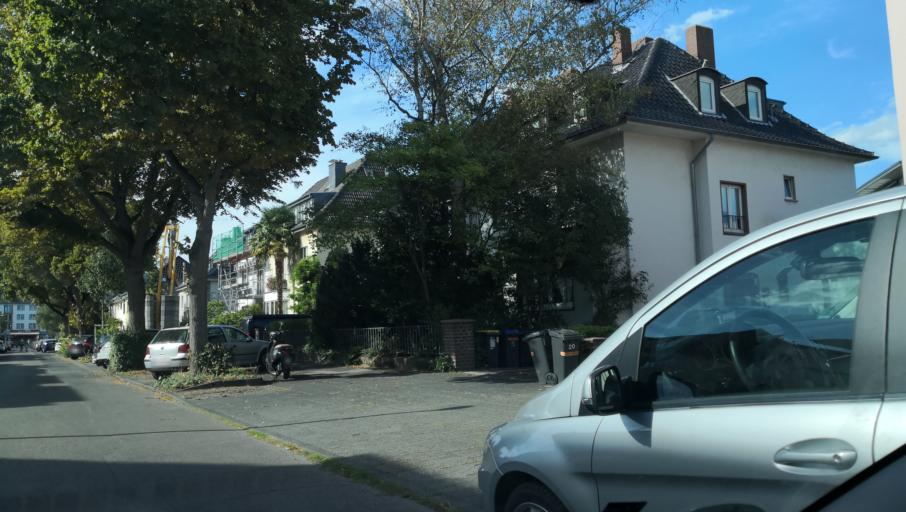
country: DE
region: North Rhine-Westphalia
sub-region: Regierungsbezirk Koln
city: Neustadt/Sued
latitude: 50.9153
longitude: 6.9094
